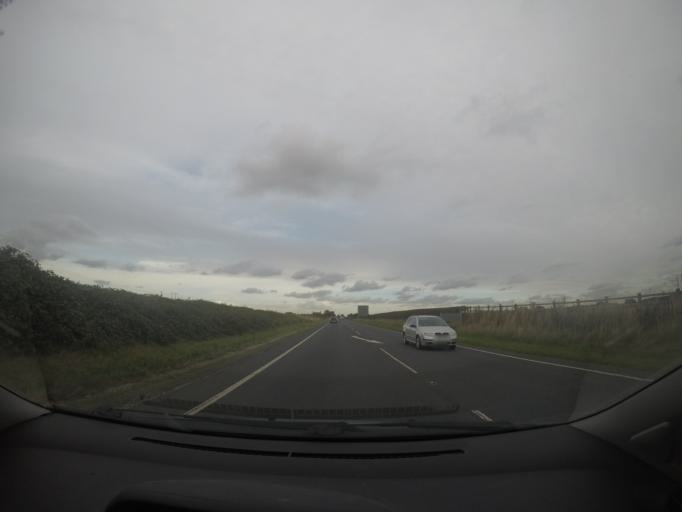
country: GB
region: England
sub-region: North Yorkshire
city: Barlby
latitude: 53.8109
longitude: -1.0396
